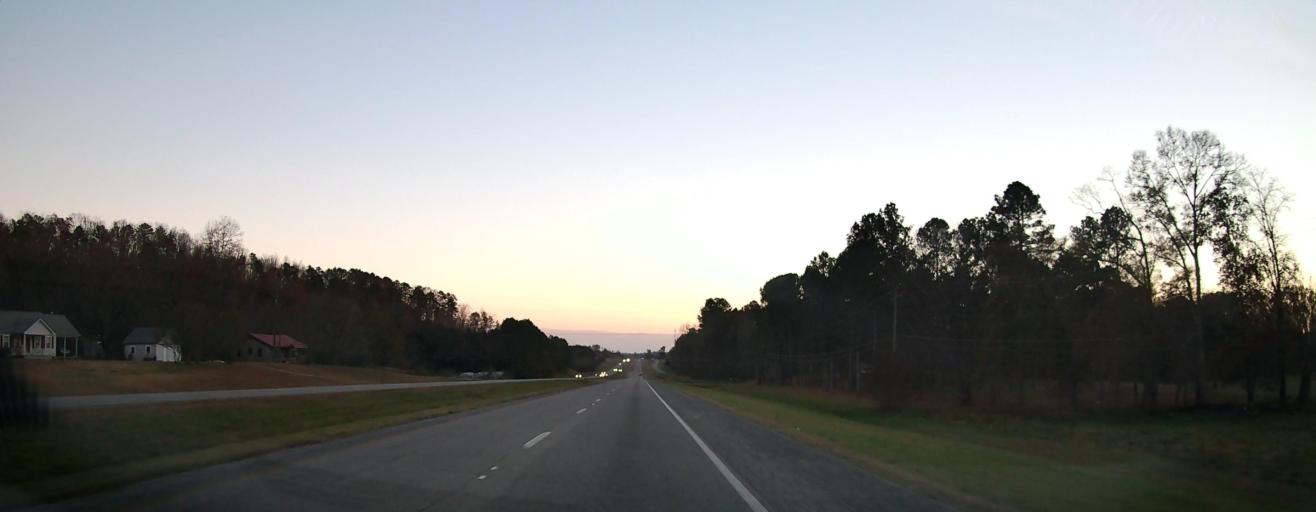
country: US
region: Alabama
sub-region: Calhoun County
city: Alexandria
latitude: 33.8344
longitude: -85.9132
